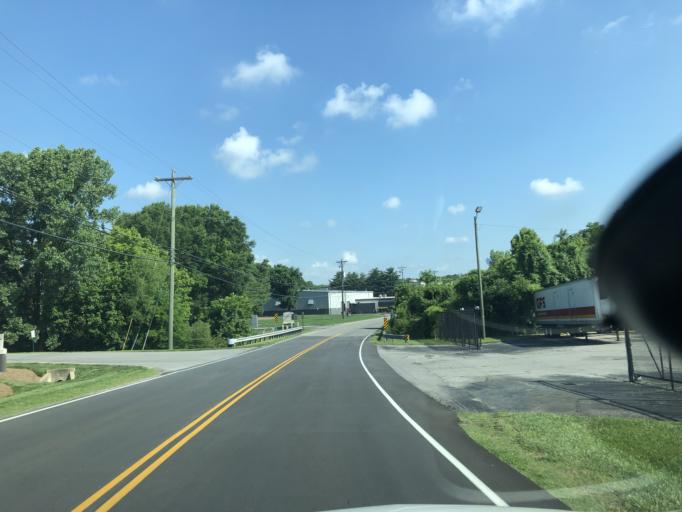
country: US
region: Tennessee
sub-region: Rutherford County
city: La Vergne
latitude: 36.0094
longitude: -86.6120
